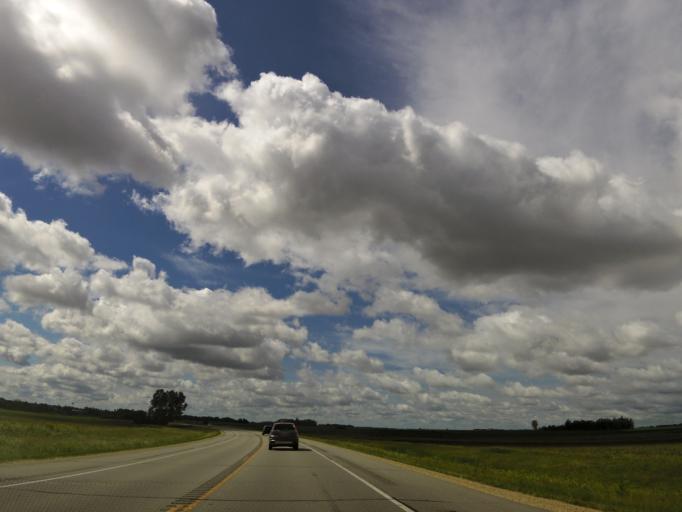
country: US
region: Minnesota
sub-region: Olmsted County
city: Stewartville
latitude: 43.7931
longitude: -92.4913
